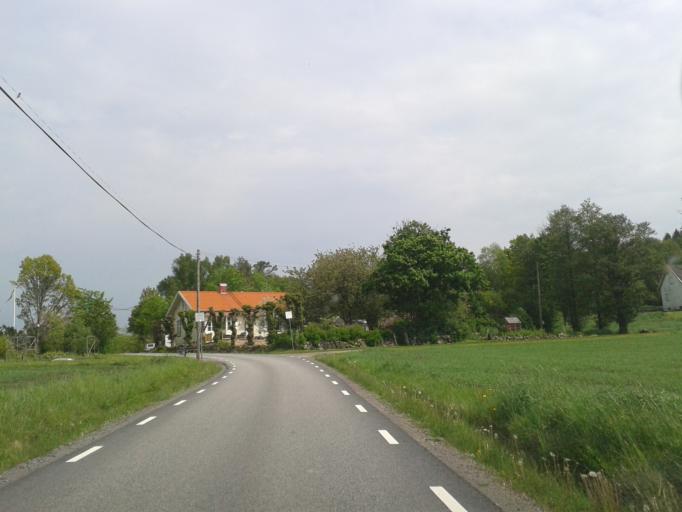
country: SE
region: Vaestra Goetaland
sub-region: Kungalvs Kommun
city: Kungalv
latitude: 57.9185
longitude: 11.9523
